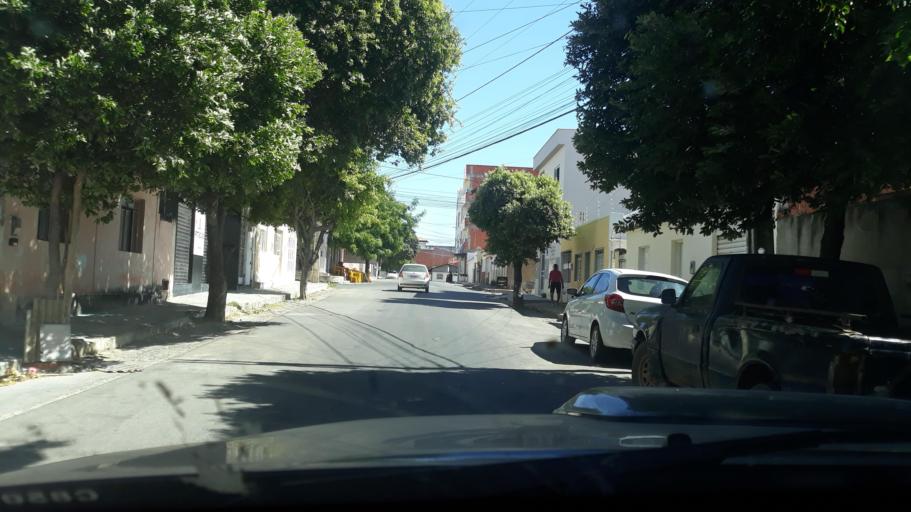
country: BR
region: Bahia
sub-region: Guanambi
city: Guanambi
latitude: -14.2208
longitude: -42.7837
